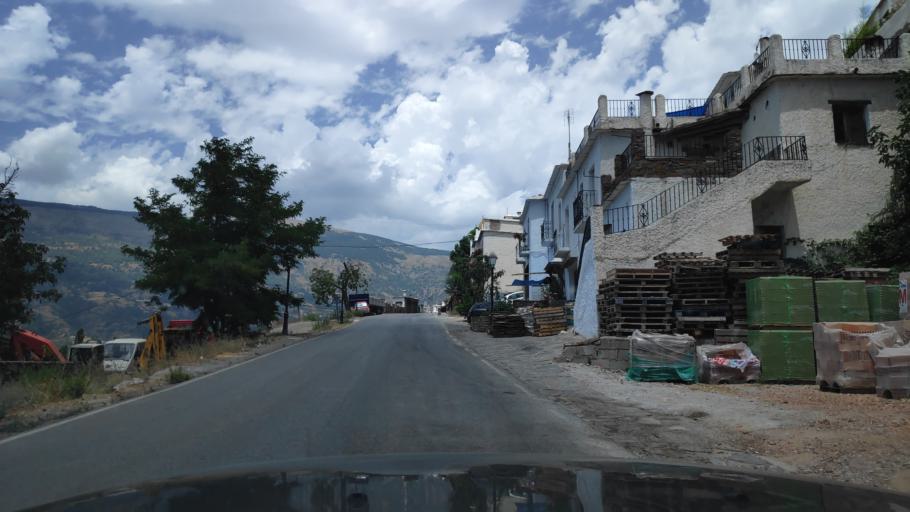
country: ES
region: Andalusia
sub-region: Provincia de Granada
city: Bubion
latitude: 36.9461
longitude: -3.3540
